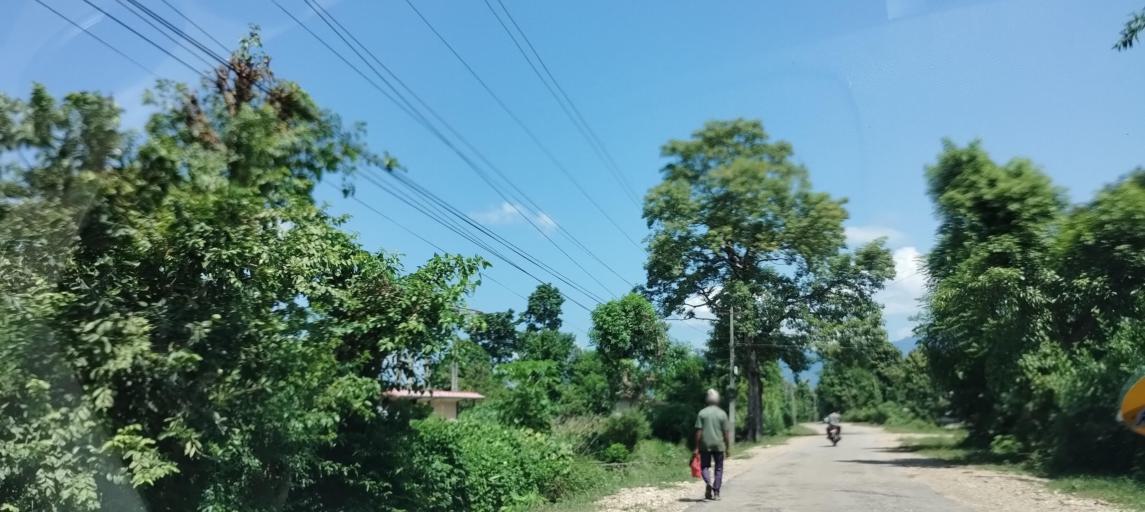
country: NP
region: Far Western
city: Tikapur
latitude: 28.5060
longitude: 81.3028
